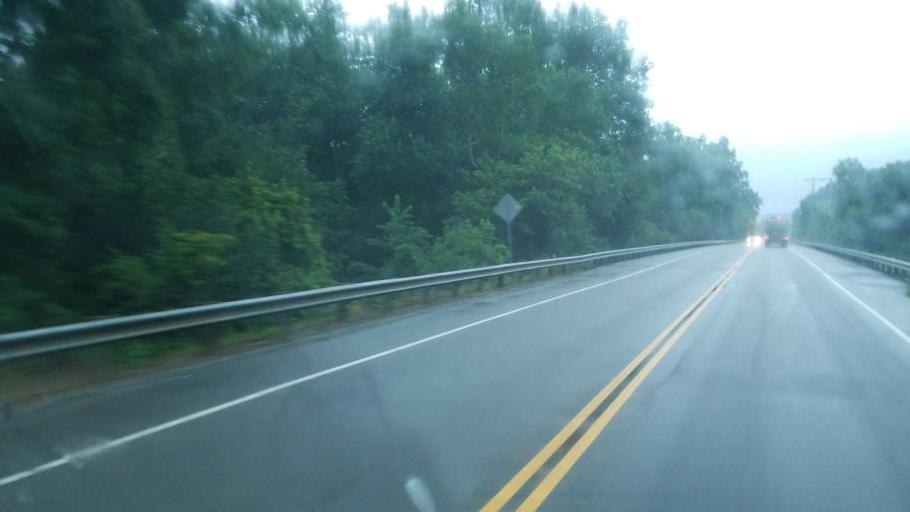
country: US
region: Ohio
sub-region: Coshocton County
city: Coshocton
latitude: 40.3282
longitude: -81.9437
